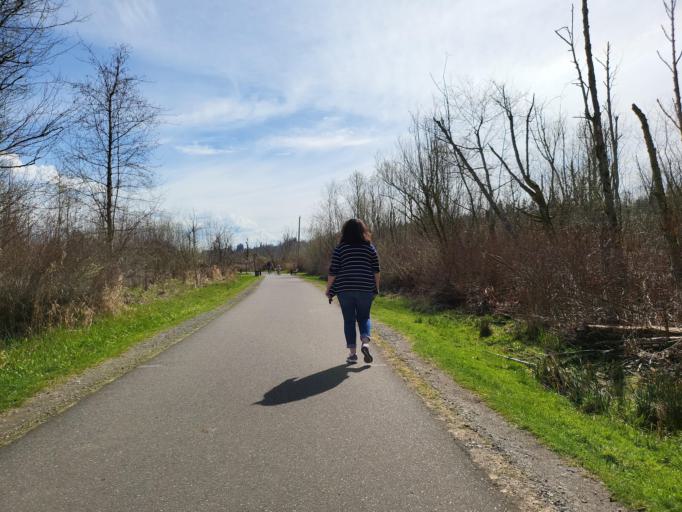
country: US
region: Washington
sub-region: King County
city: East Hill-Meridian
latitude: 47.4093
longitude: -122.1594
